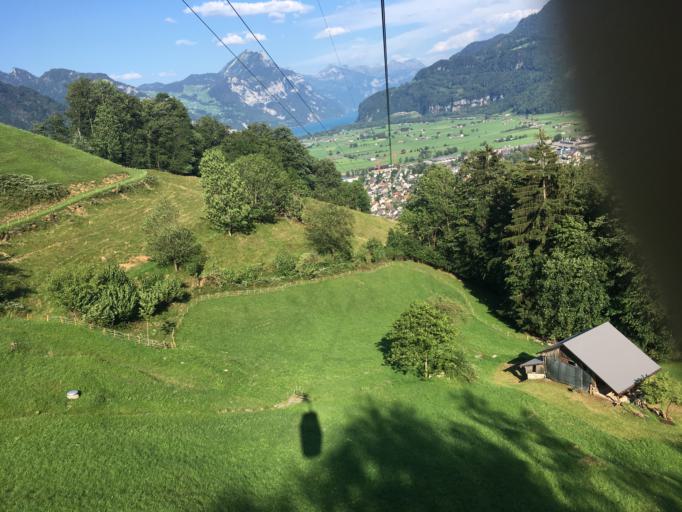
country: CH
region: Glarus
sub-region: Glarus
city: Niederurnen
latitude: 47.1251
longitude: 9.0381
